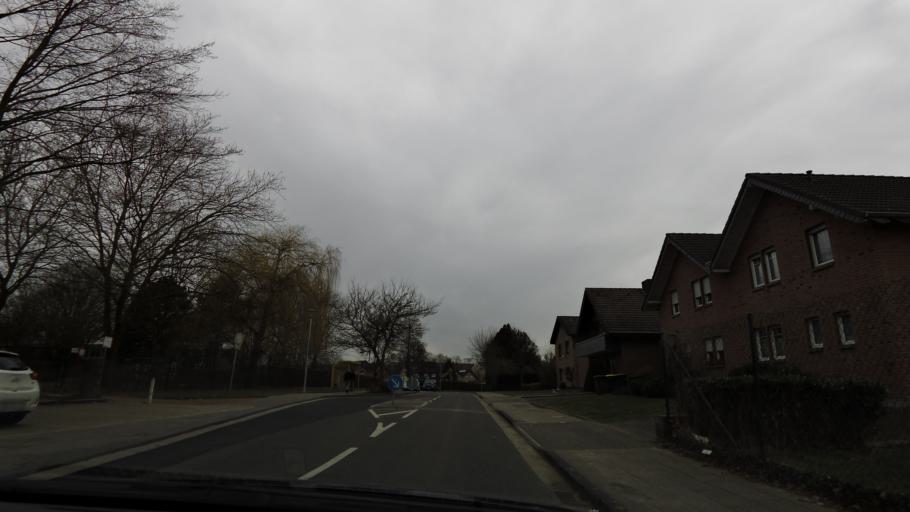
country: DE
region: North Rhine-Westphalia
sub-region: Regierungsbezirk Koln
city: Ubach-Palenberg
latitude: 50.9197
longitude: 6.1100
